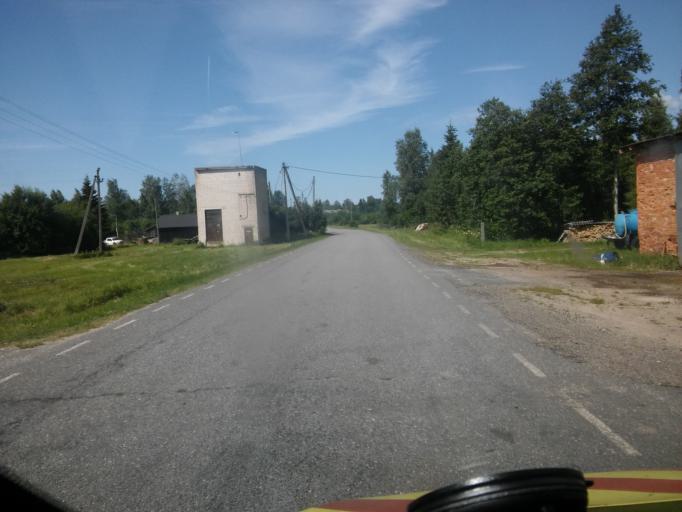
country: EE
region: Paernumaa
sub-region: Sindi linn
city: Sindi
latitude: 58.2491
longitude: 24.7534
